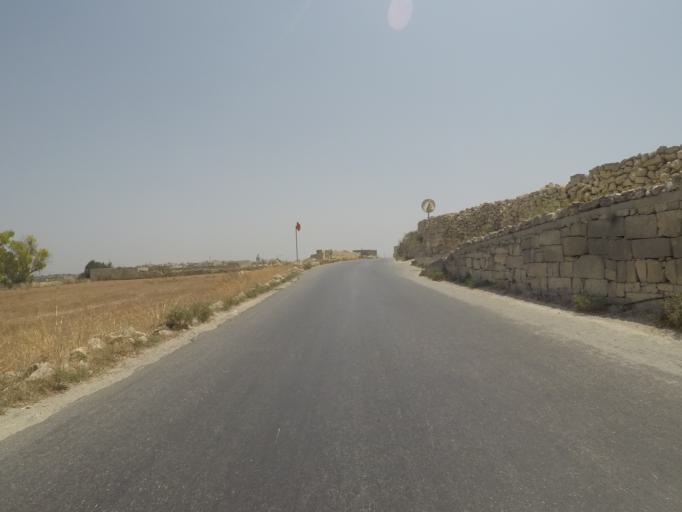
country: MT
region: Is-Siggiewi
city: Siggiewi
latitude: 35.8560
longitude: 14.4242
